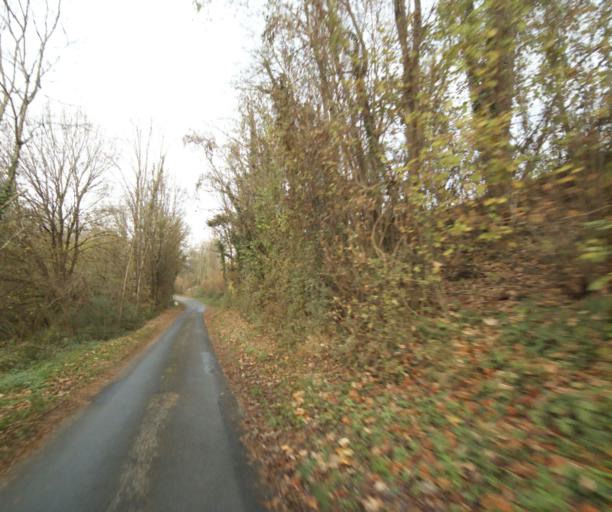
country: FR
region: Poitou-Charentes
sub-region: Departement de la Charente-Maritime
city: Fontcouverte
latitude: 45.7755
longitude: -0.5867
